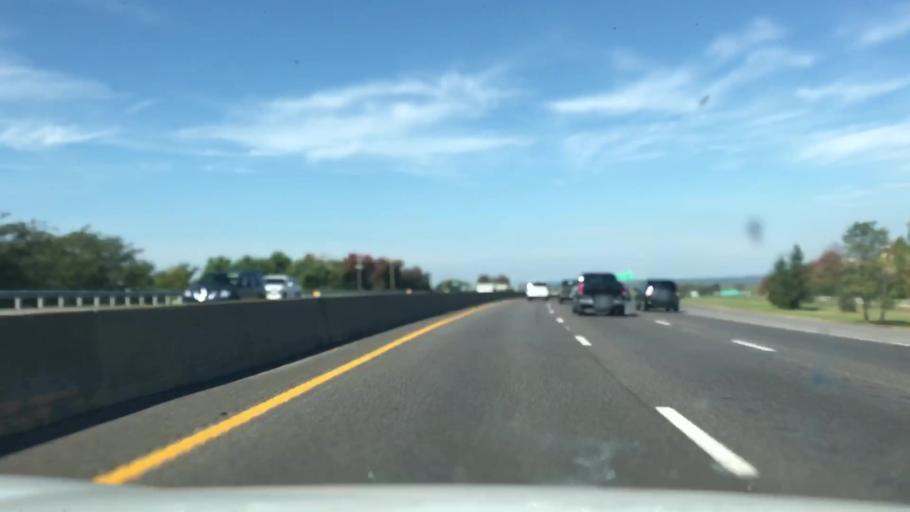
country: US
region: Missouri
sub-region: Saint Louis County
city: Chesterfield
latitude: 38.6532
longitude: -90.5589
